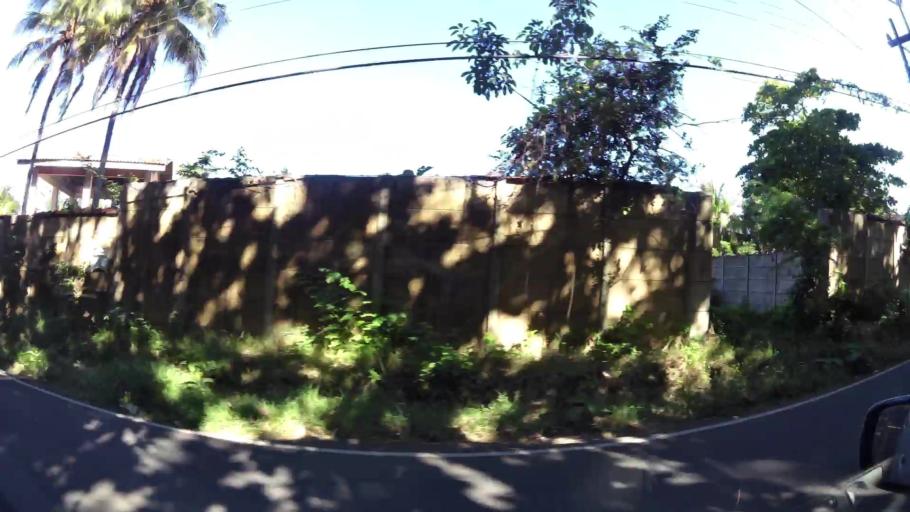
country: CR
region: Guanacaste
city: Sardinal
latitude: 10.4399
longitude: -85.7761
